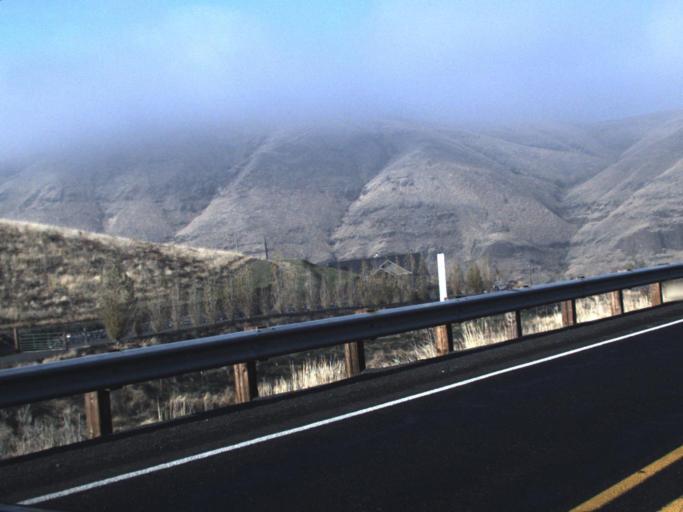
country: US
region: Washington
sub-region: Asotin County
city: Asotin
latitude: 46.3327
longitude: -117.0570
